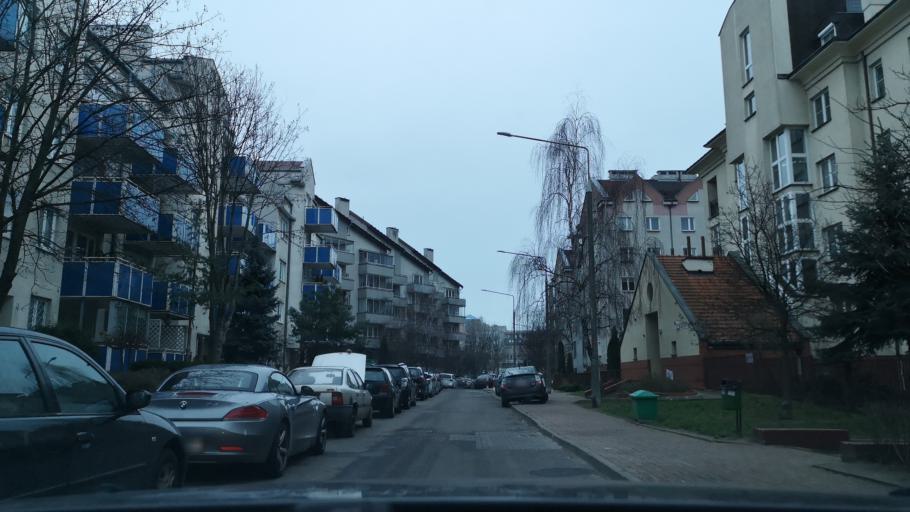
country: PL
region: Masovian Voivodeship
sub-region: Warszawa
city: Bemowo
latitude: 52.2431
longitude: 20.9184
